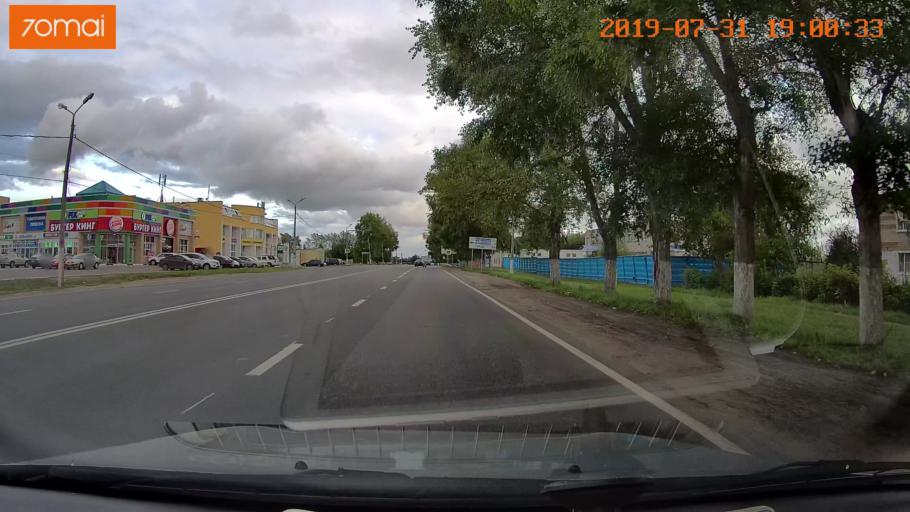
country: RU
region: Moskovskaya
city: Raduzhnyy
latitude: 55.1325
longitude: 38.7251
